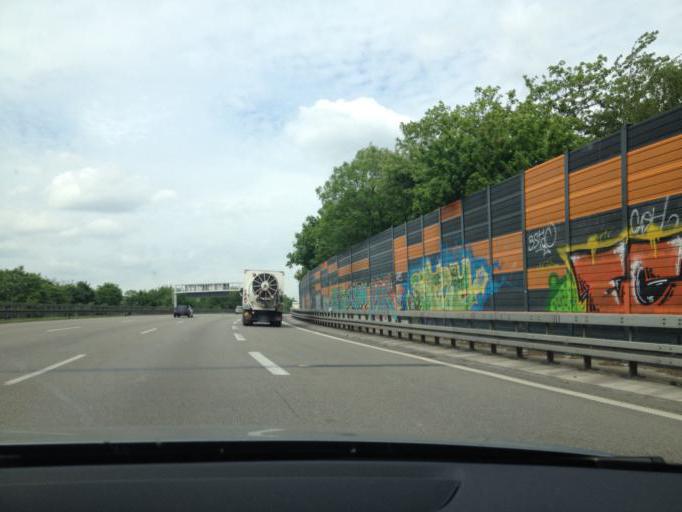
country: DE
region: North Rhine-Westphalia
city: Meiderich
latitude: 51.4847
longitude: 6.7959
